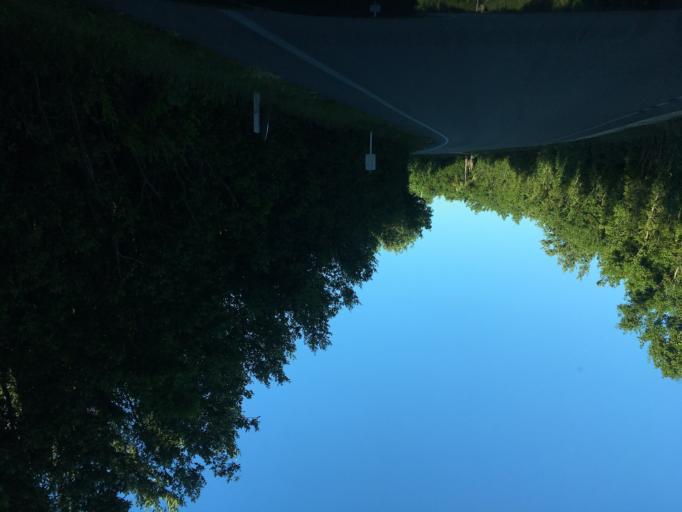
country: US
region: Florida
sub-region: Lee County
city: Pine Island Center
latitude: 26.5322
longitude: -82.1939
